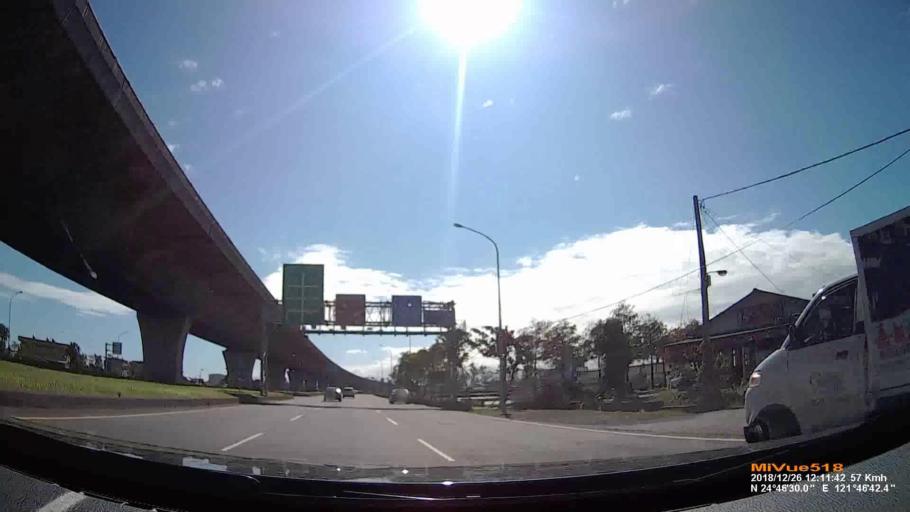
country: TW
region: Taiwan
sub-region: Yilan
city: Yilan
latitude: 24.7780
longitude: 121.7594
